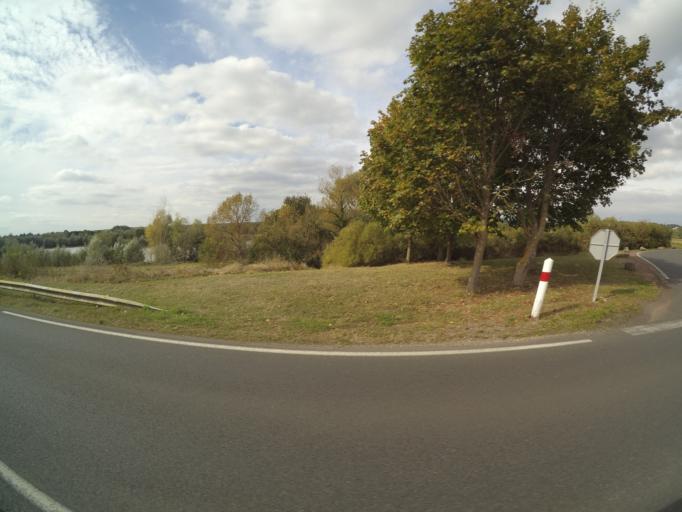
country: FR
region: Centre
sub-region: Departement d'Indre-et-Loire
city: Cinq-Mars-la-Pile
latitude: 47.3348
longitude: 0.4608
